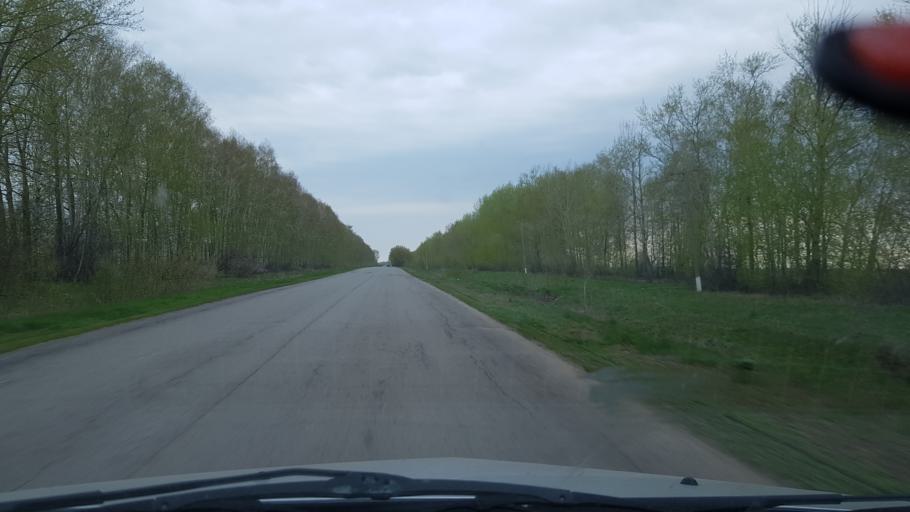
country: RU
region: Samara
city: Podstepki
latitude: 53.6643
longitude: 49.1817
